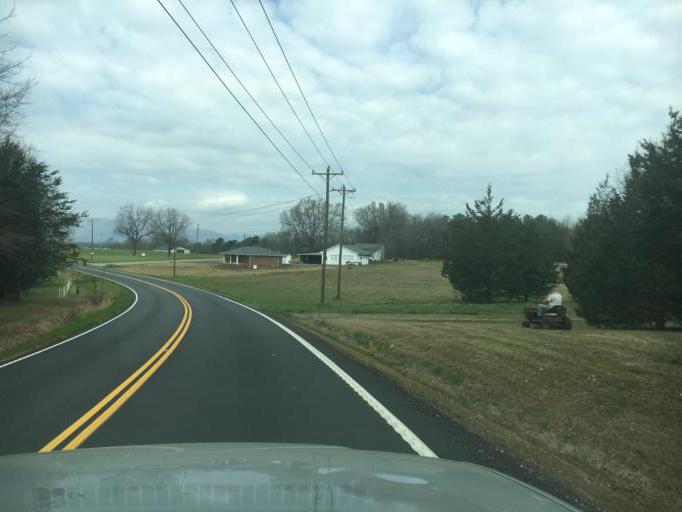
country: US
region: South Carolina
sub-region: Spartanburg County
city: Inman Mills
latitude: 35.0772
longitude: -82.1819
